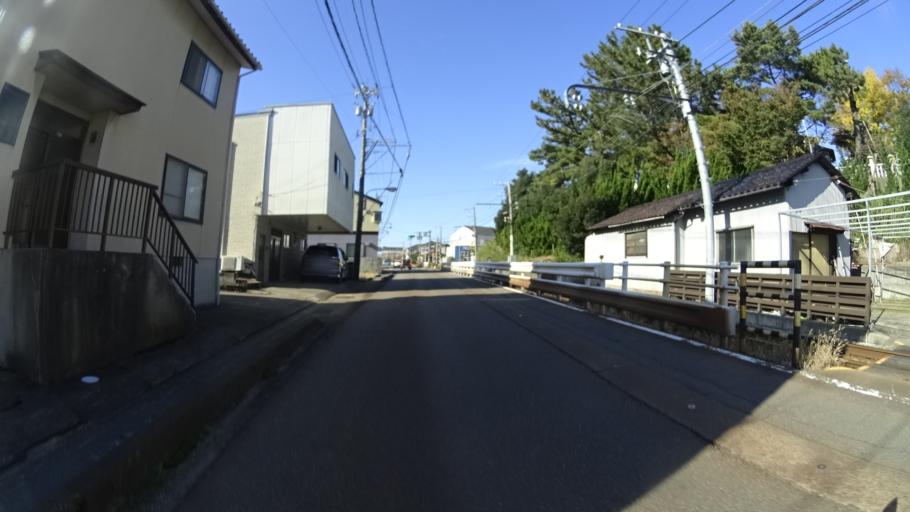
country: JP
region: Ishikawa
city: Kanazawa-shi
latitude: 36.6307
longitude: 136.6375
